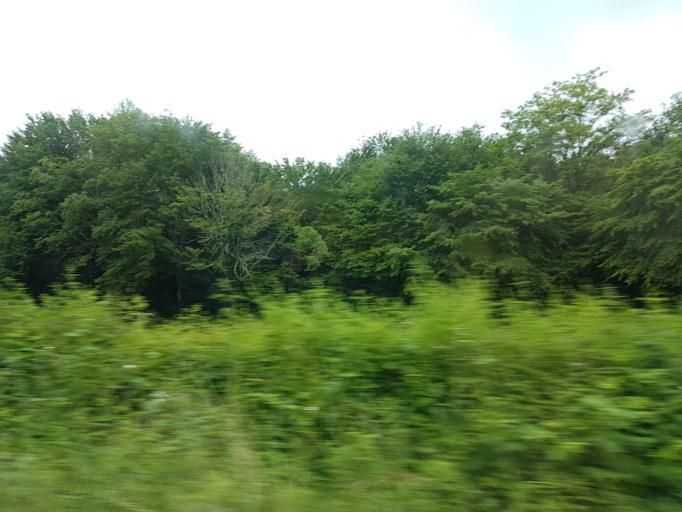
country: FR
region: Bourgogne
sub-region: Departement de la Nievre
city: Corbigny
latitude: 47.2070
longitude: 3.7170
